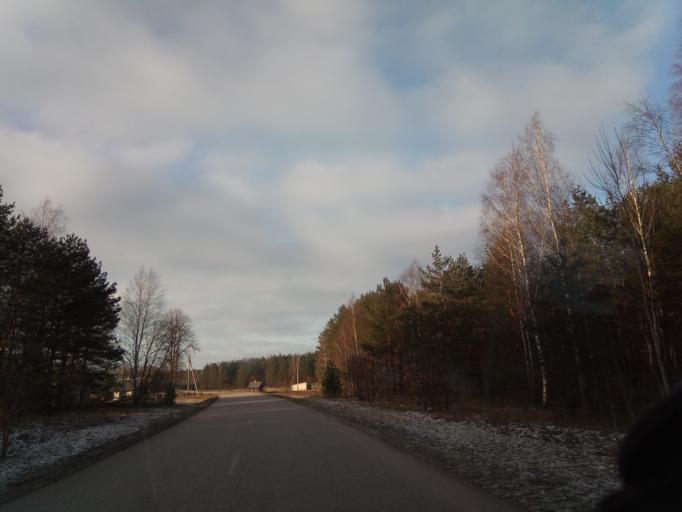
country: LT
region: Alytaus apskritis
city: Druskininkai
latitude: 53.9812
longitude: 24.2426
